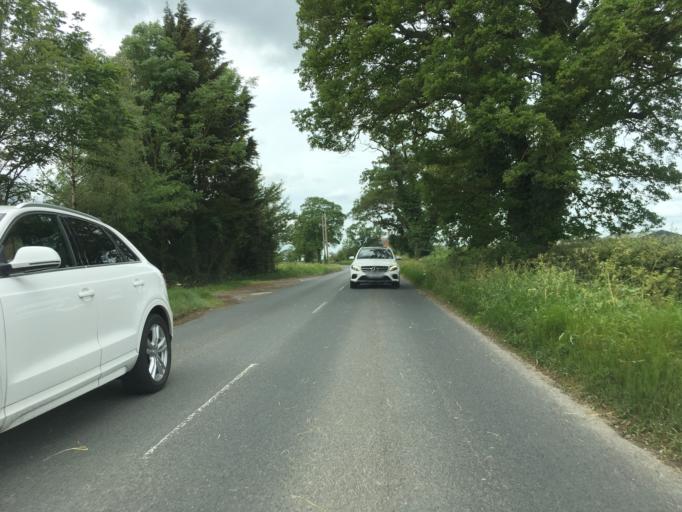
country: GB
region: England
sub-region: Wiltshire
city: Royal Wootton Bassett
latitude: 51.5612
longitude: -1.9304
